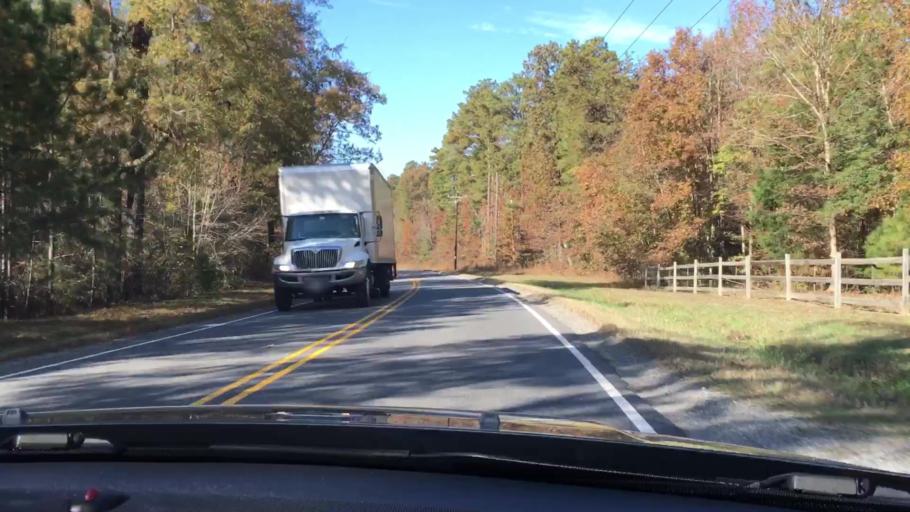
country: US
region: Virginia
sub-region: King and Queen County
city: King and Queen Court House
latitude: 37.6498
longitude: -76.9427
